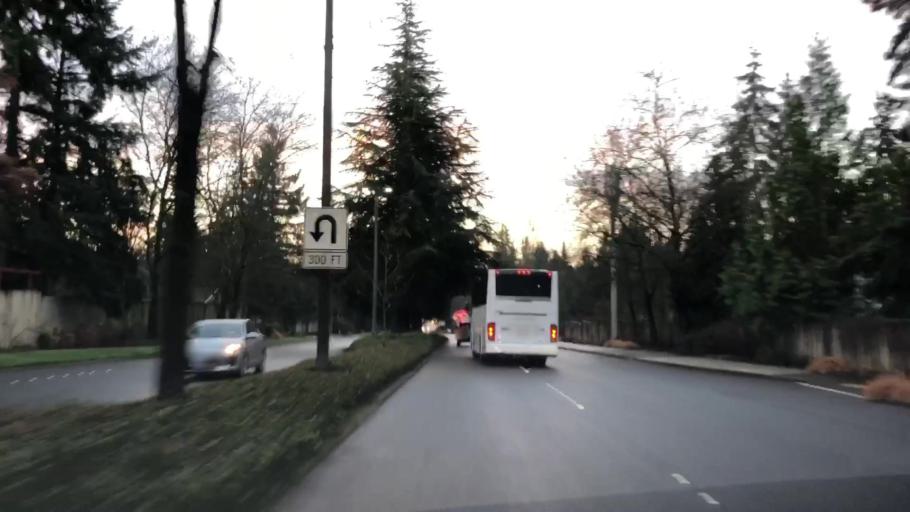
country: US
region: Washington
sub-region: King County
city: Eastgate
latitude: 47.6221
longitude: -122.1433
